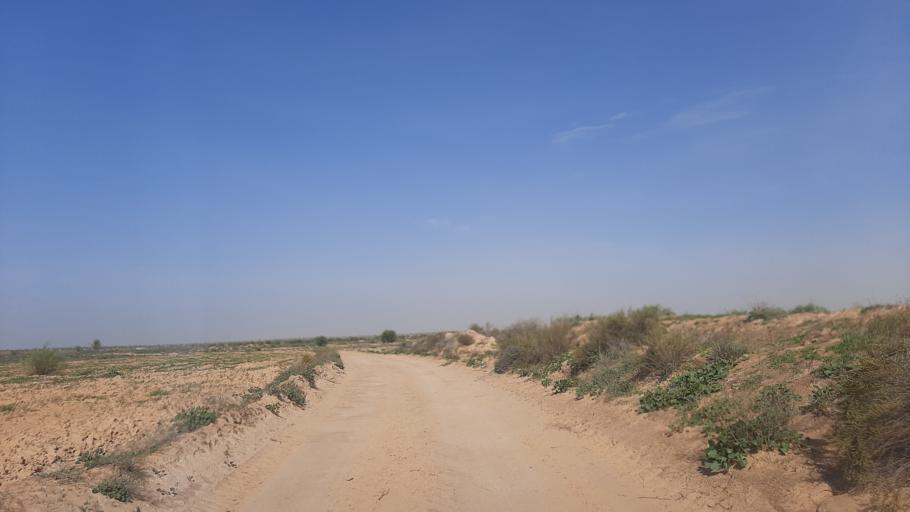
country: TN
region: Madanin
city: Zarzis
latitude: 33.4425
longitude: 10.8085
